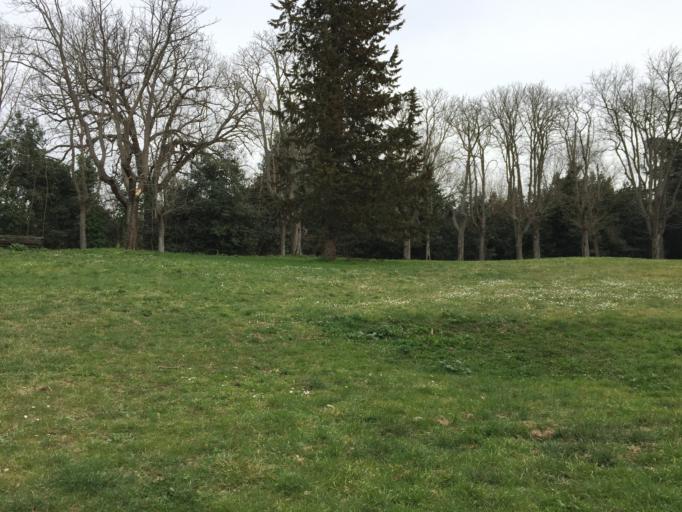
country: VA
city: Vatican City
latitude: 41.8827
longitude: 12.4470
